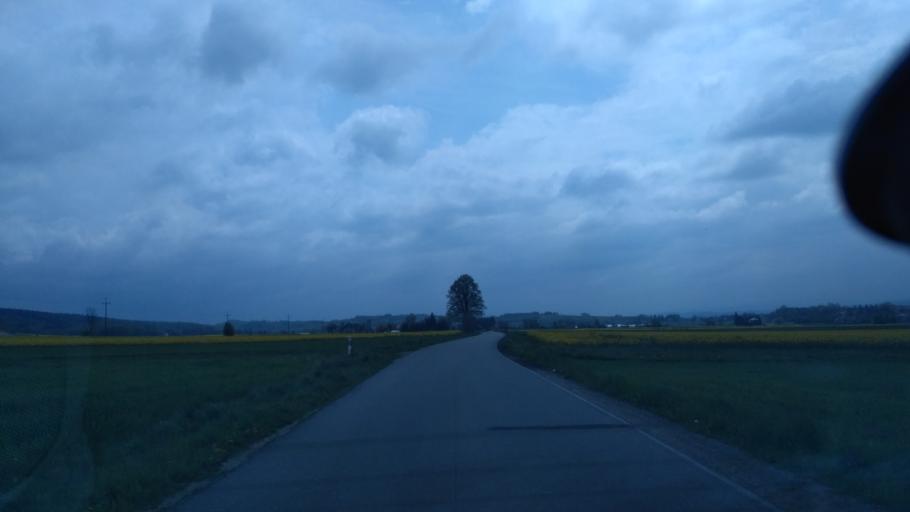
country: PL
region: Subcarpathian Voivodeship
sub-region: Powiat brzozowski
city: Jablonica Polska
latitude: 49.6846
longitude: 21.8961
